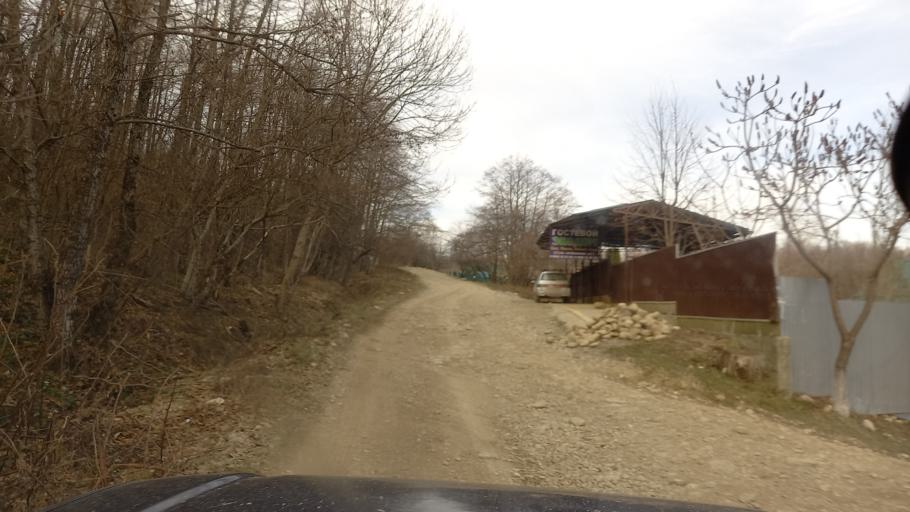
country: RU
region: Krasnodarskiy
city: Neftegorsk
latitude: 44.2271
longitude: 39.8997
